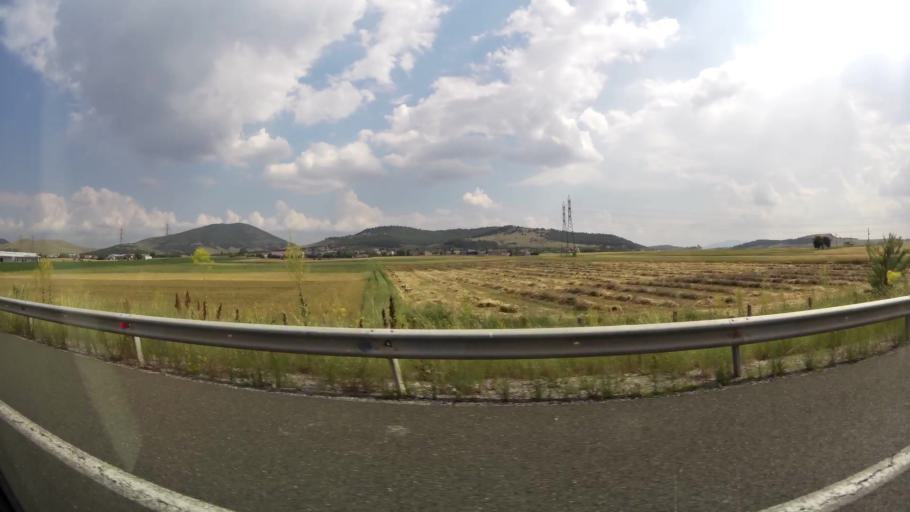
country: GR
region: West Macedonia
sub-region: Nomos Kozanis
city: Koila
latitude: 40.3614
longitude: 21.8374
